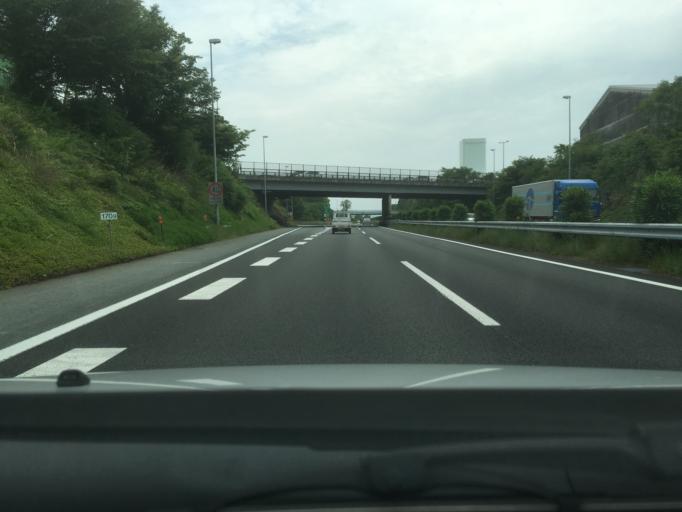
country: JP
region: Kumamoto
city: Kumamoto
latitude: 32.8375
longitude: 130.7775
